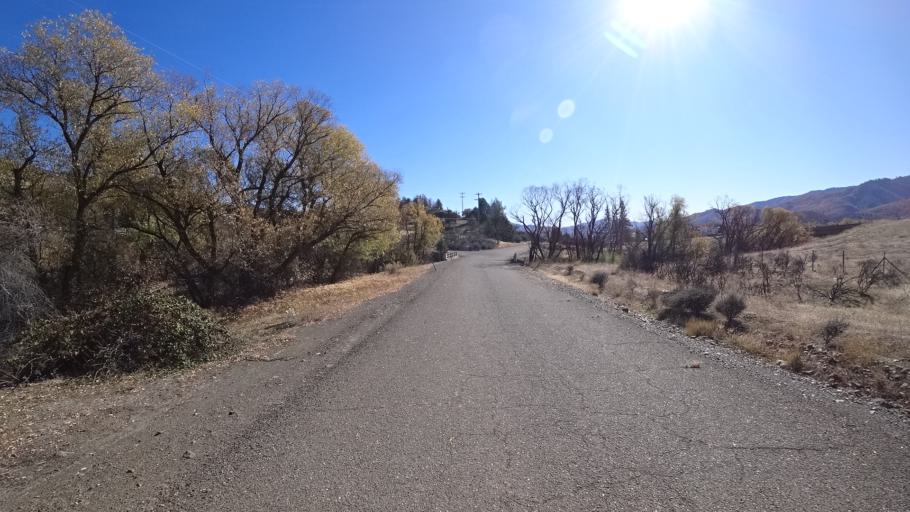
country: US
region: California
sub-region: Siskiyou County
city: Yreka
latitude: 41.9465
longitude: -122.5865
